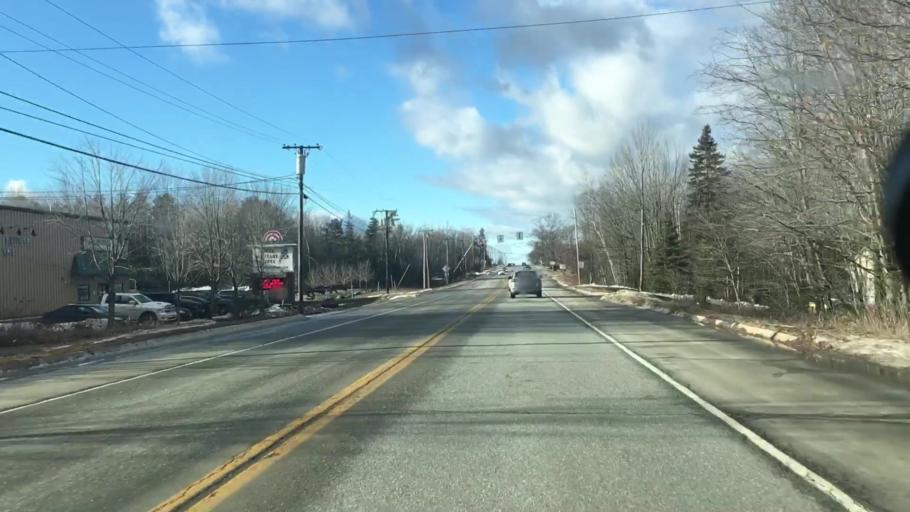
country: US
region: Maine
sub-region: Penobscot County
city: Holden
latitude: 44.7611
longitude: -68.6973
